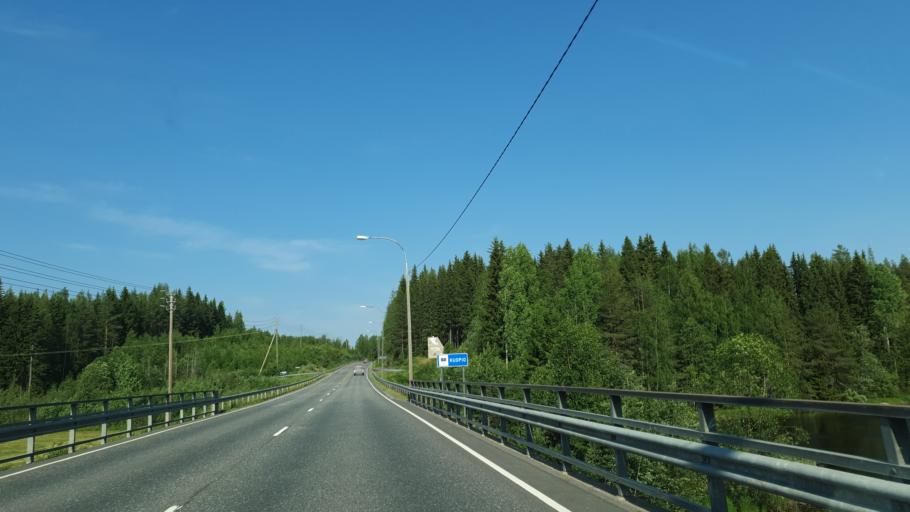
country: FI
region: Northern Savo
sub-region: Kuopio
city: Siilinjaervi
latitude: 63.1352
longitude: 27.8265
